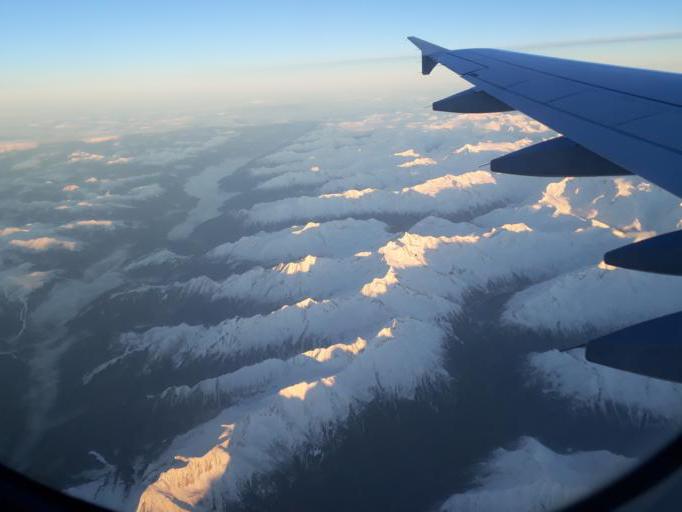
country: AT
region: Tyrol
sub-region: Politischer Bezirk Schwaz
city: Mayrhofen
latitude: 47.1352
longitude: 11.8808
